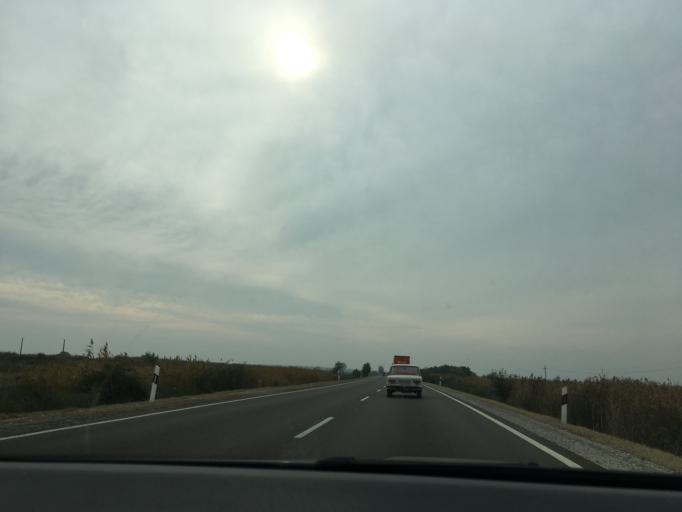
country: HU
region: Jasz-Nagykun-Szolnok
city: Kisujszallas
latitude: 47.2389
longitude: 20.8251
